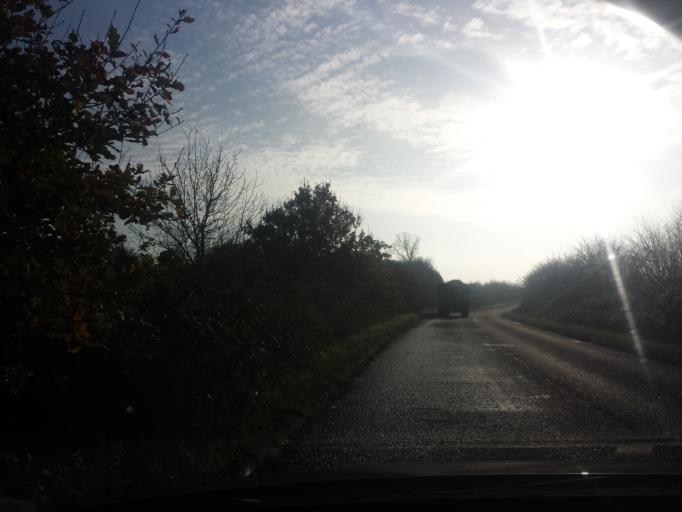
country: GB
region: England
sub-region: Essex
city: Little Clacton
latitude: 51.8411
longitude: 1.1233
